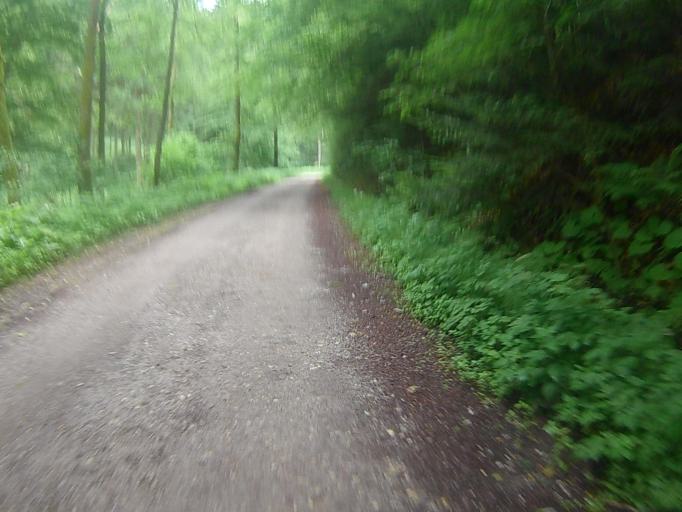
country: SI
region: Maribor
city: Bresternica
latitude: 46.6008
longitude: 15.5872
